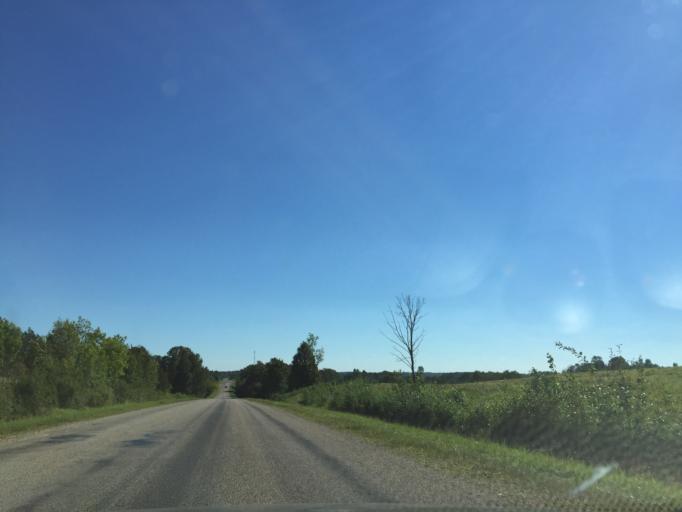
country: LV
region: Akniste
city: Akniste
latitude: 56.0287
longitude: 25.9153
